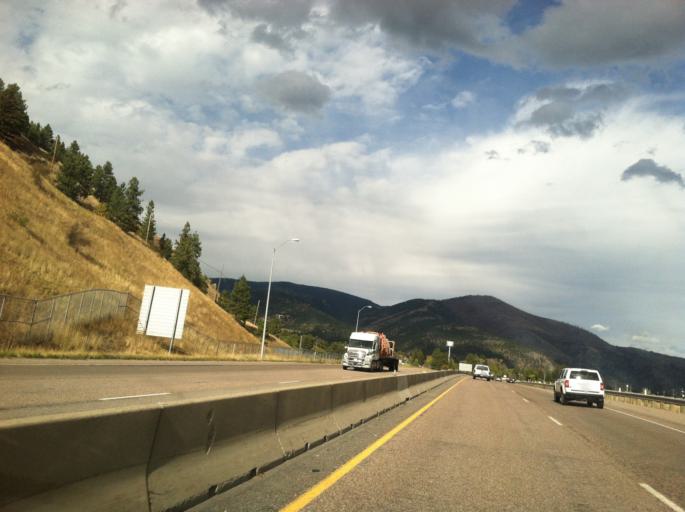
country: US
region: Montana
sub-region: Missoula County
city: East Missoula
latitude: 46.8656
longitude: -113.9539
